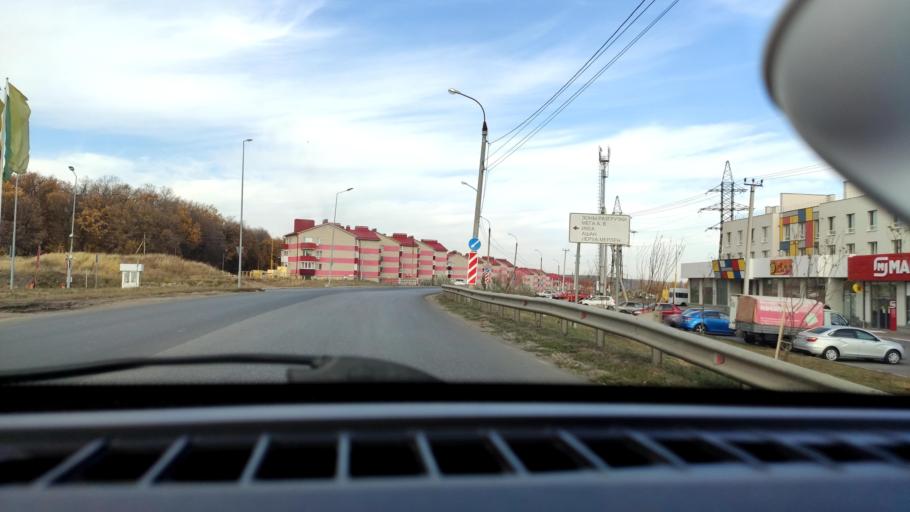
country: RU
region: Samara
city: Novosemeykino
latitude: 53.3271
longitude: 50.3111
